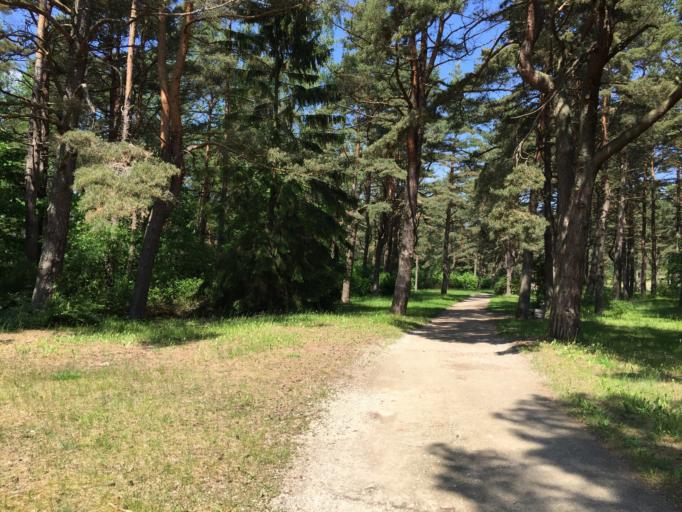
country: LT
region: Klaipedos apskritis
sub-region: Klaipeda
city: Palanga
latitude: 55.9030
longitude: 21.0526
